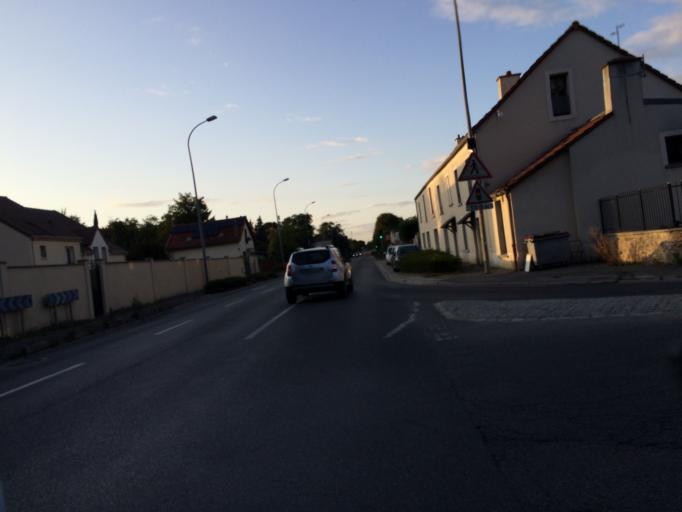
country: FR
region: Ile-de-France
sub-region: Departement de l'Essonne
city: Orsay
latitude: 48.6678
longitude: 2.1968
